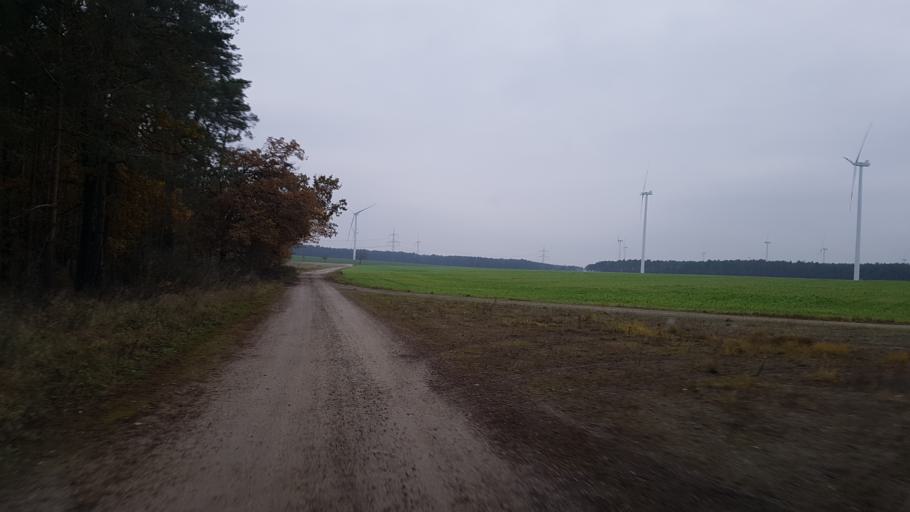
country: DE
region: Brandenburg
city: Schilda
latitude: 51.6515
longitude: 13.3807
